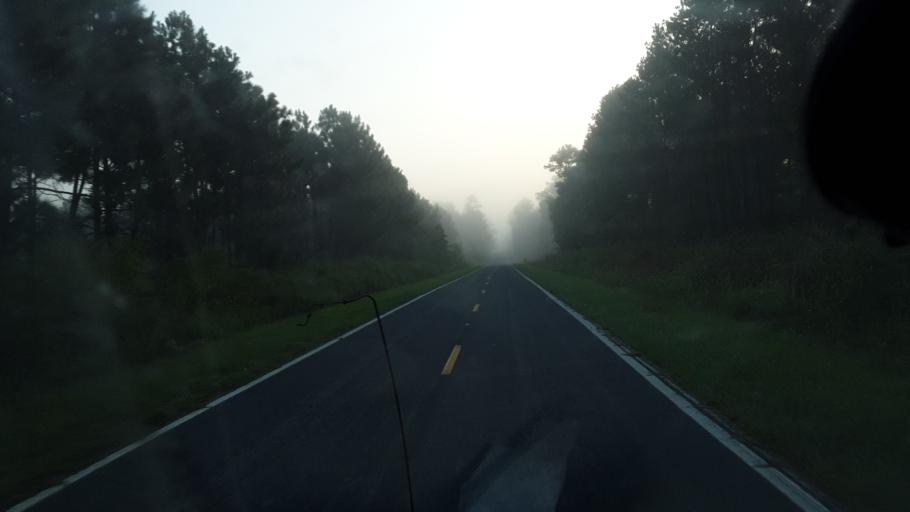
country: US
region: South Carolina
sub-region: Clarendon County
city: Manning
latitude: 33.7641
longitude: -80.0459
